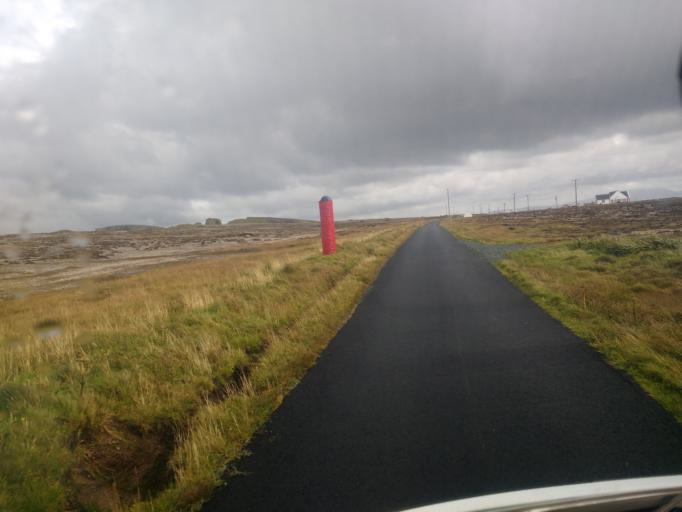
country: IE
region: Ulster
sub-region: County Donegal
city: Derrybeg
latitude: 55.2626
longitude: -8.2167
